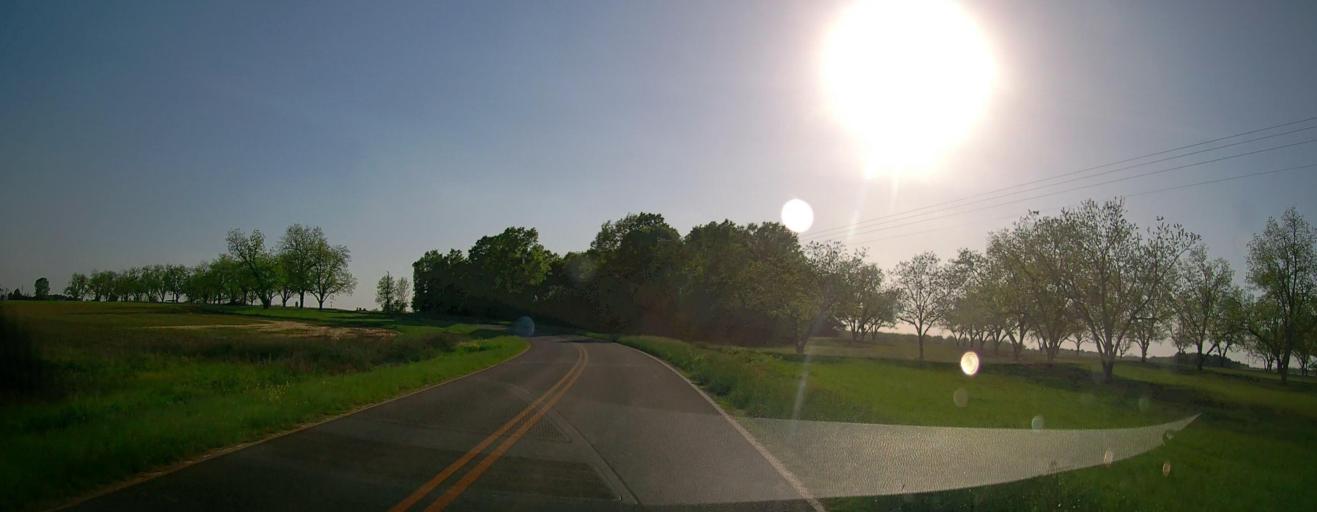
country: US
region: Georgia
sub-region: Macon County
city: Montezuma
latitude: 32.3311
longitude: -83.9598
